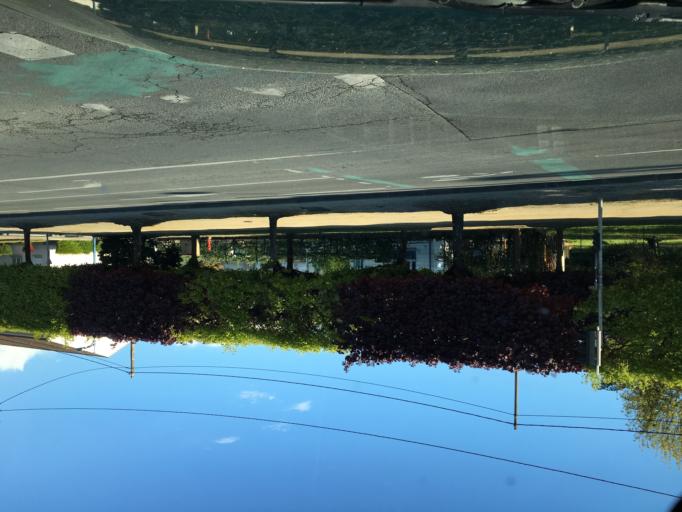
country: FR
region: Centre
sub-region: Departement du Loiret
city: Fleury-les-Aubrais
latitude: 47.9343
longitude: 1.9034
